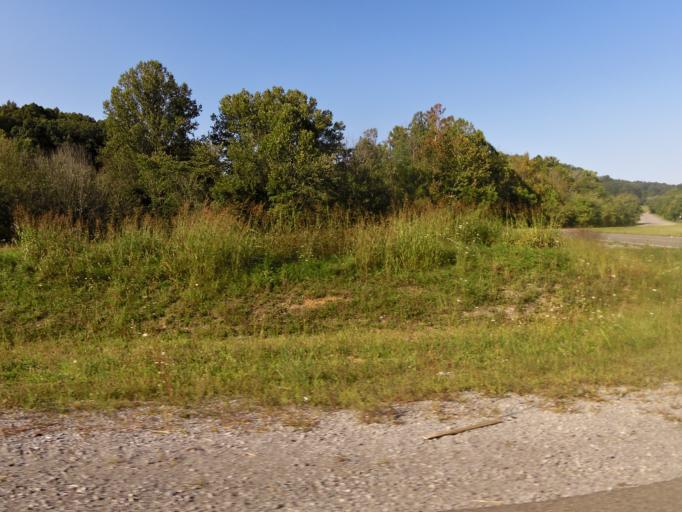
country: US
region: Tennessee
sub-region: Claiborne County
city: New Tazewell
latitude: 36.3960
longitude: -83.6840
